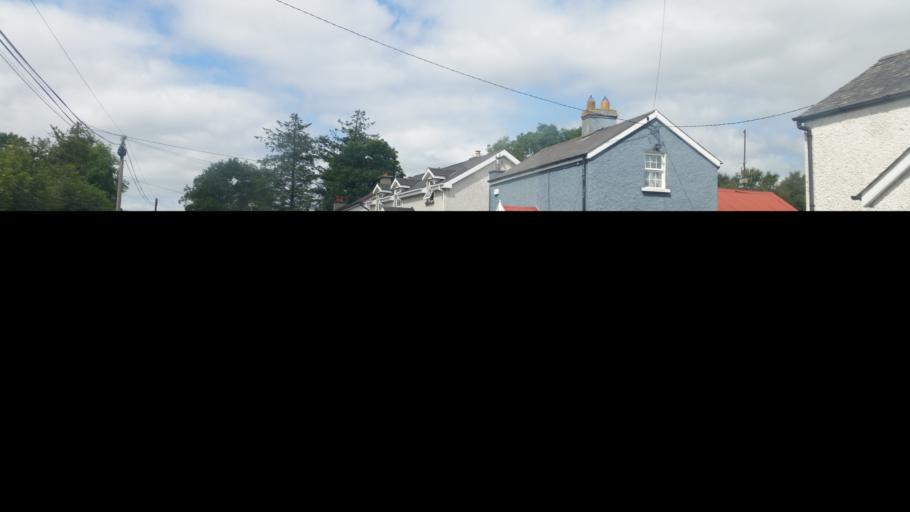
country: IE
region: Leinster
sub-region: County Carlow
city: Tullow
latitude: 52.8148
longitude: -6.7260
